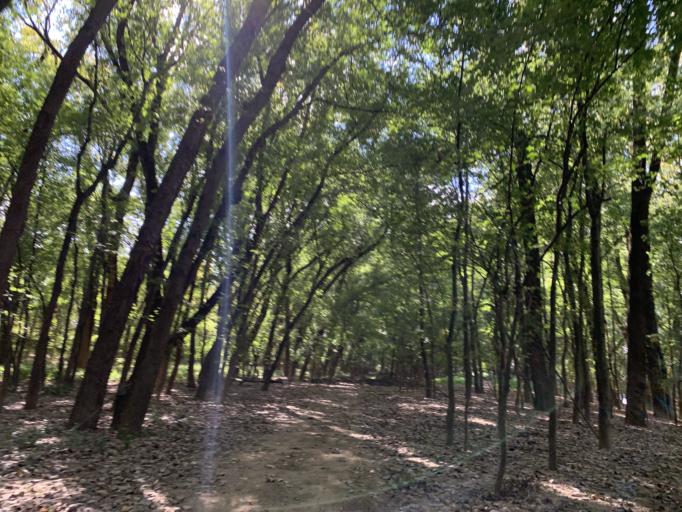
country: US
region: Indiana
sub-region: Floyd County
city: New Albany
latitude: 38.2775
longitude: -85.8171
